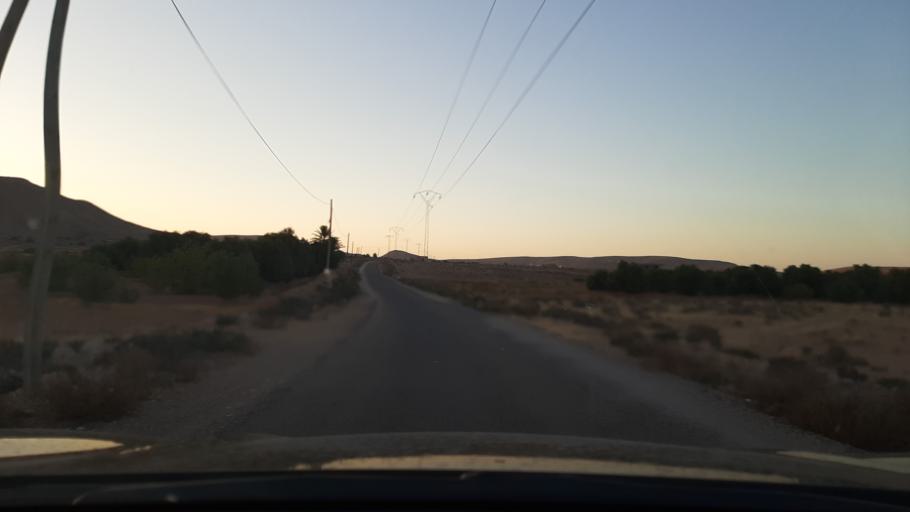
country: TN
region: Qabis
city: Matmata
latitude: 33.5477
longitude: 10.1907
